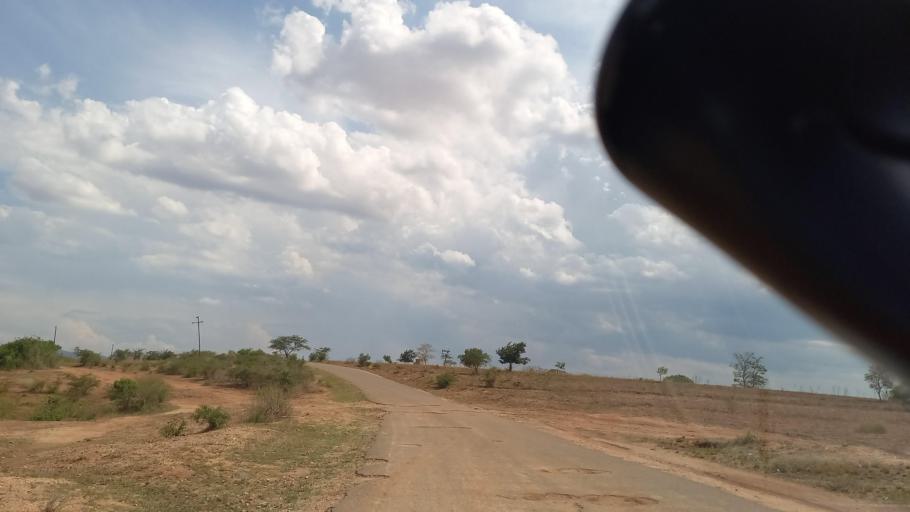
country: ZM
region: Lusaka
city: Kafue
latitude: -16.1845
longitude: 28.0870
